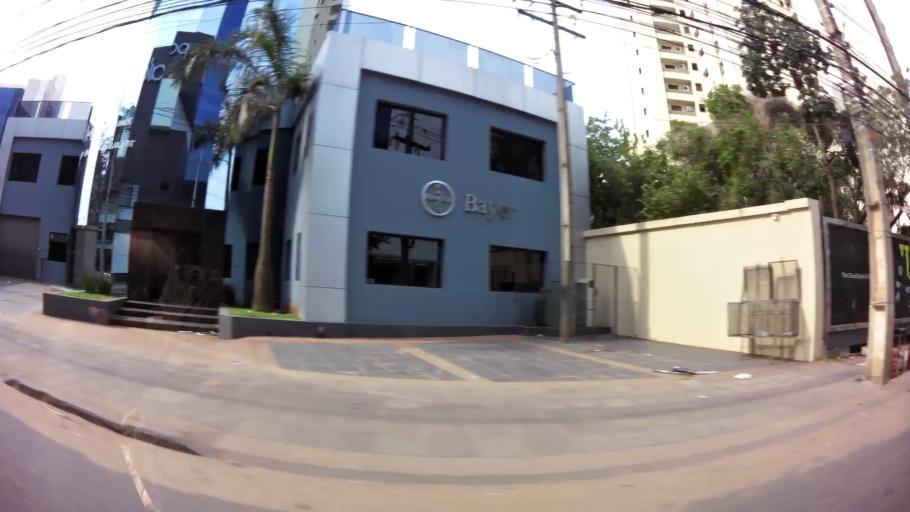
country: PY
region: Central
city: Fernando de la Mora
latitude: -25.2839
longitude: -57.5628
